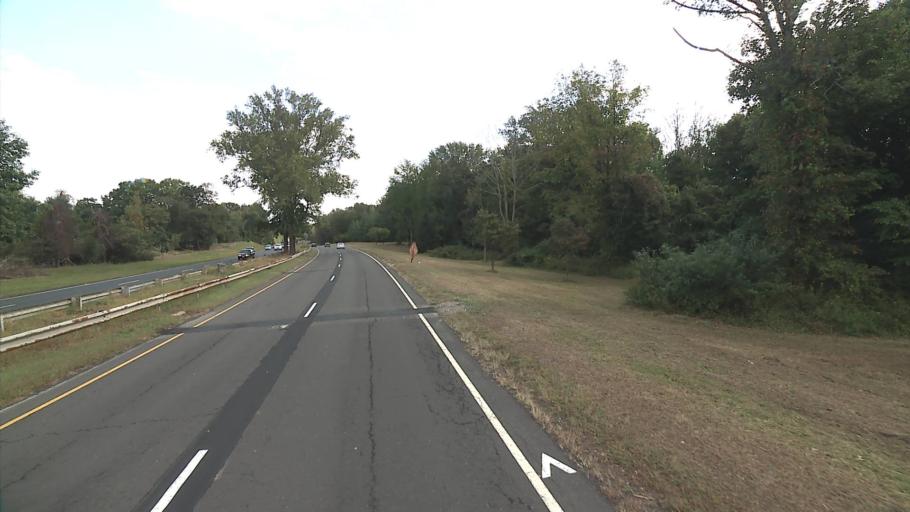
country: US
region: Connecticut
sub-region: Fairfield County
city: Westport
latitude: 41.1755
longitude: -73.3185
